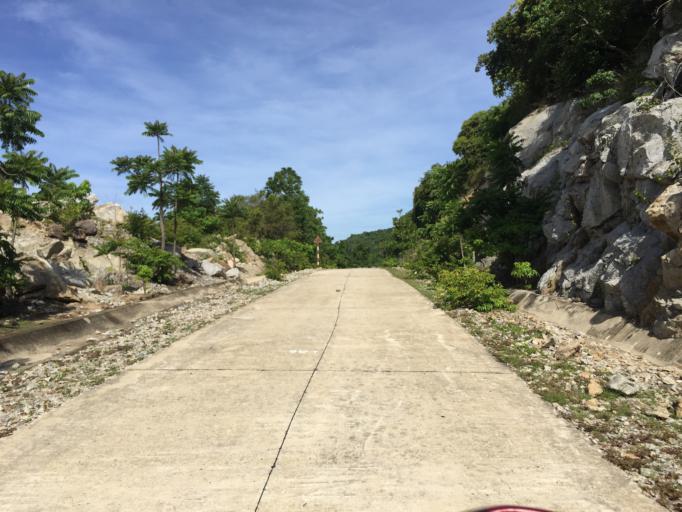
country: VN
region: Quang Nam
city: Hoi An
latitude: 15.9321
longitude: 108.5317
